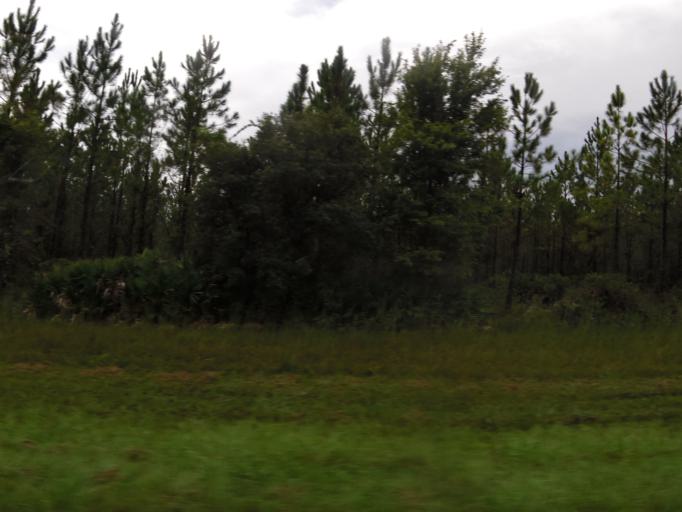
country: US
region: Florida
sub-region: Duval County
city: Baldwin
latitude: 30.3983
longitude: -81.9581
